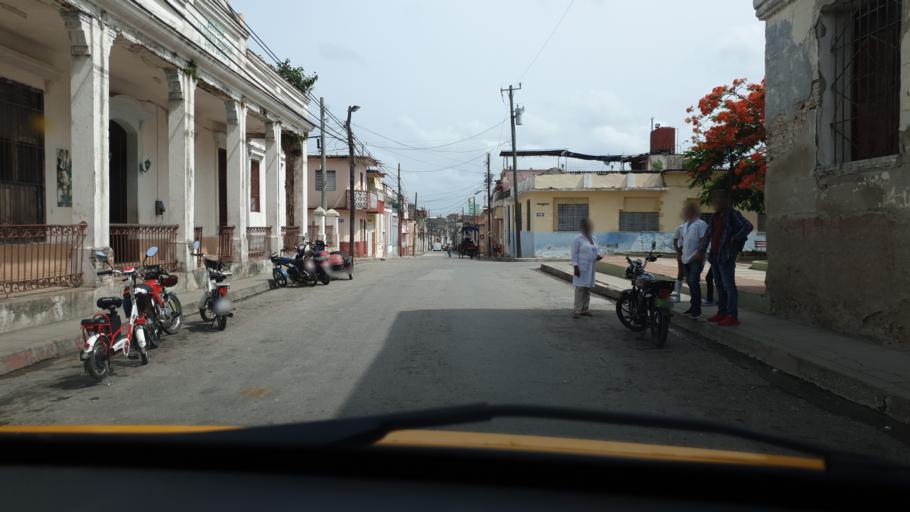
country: CU
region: Villa Clara
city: Santa Clara
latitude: 22.4018
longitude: -79.9647
